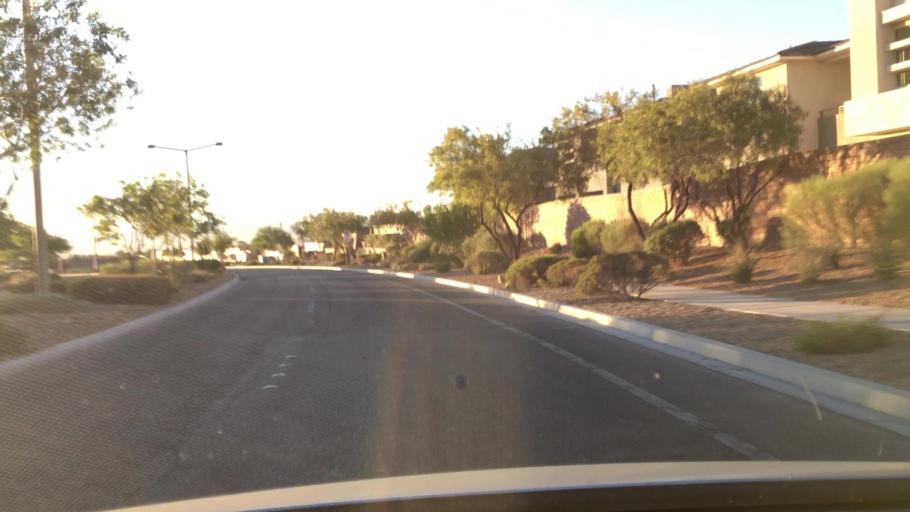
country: US
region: Nevada
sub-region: Clark County
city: Summerlin South
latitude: 36.1170
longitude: -115.3345
